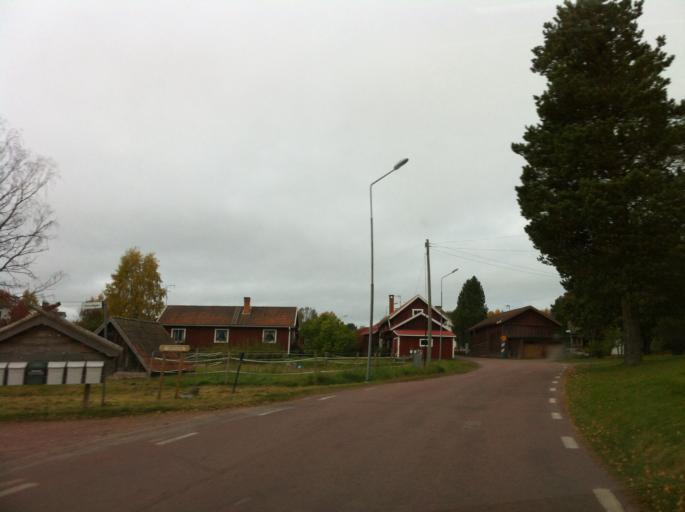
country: SE
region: Dalarna
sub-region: Mora Kommun
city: Mora
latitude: 61.1168
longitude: 14.4733
